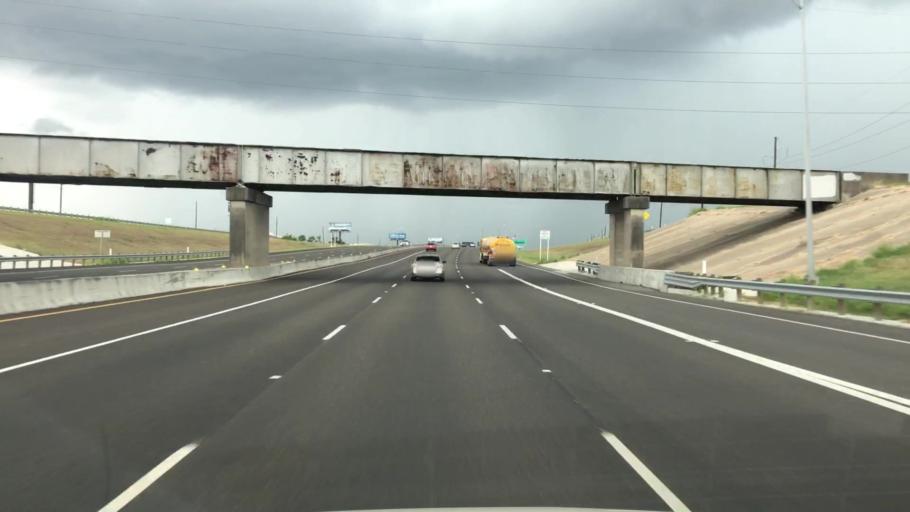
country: US
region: Texas
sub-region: Nueces County
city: Corpus Christi
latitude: 27.8059
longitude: -97.4886
